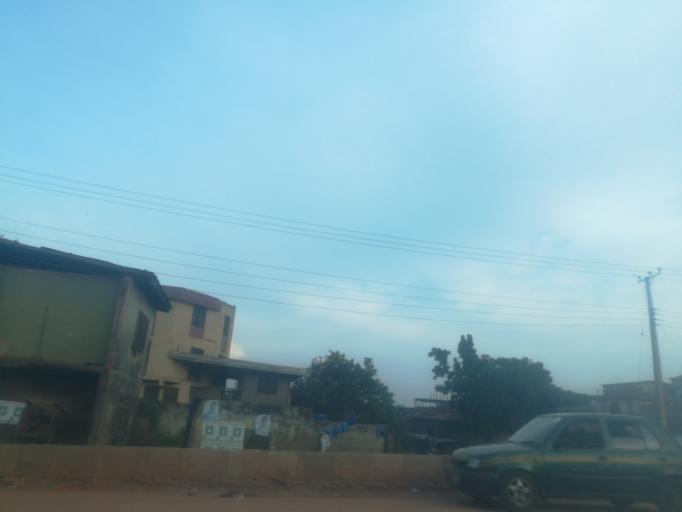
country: NG
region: Ogun
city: Abeokuta
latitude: 7.1654
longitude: 3.3356
